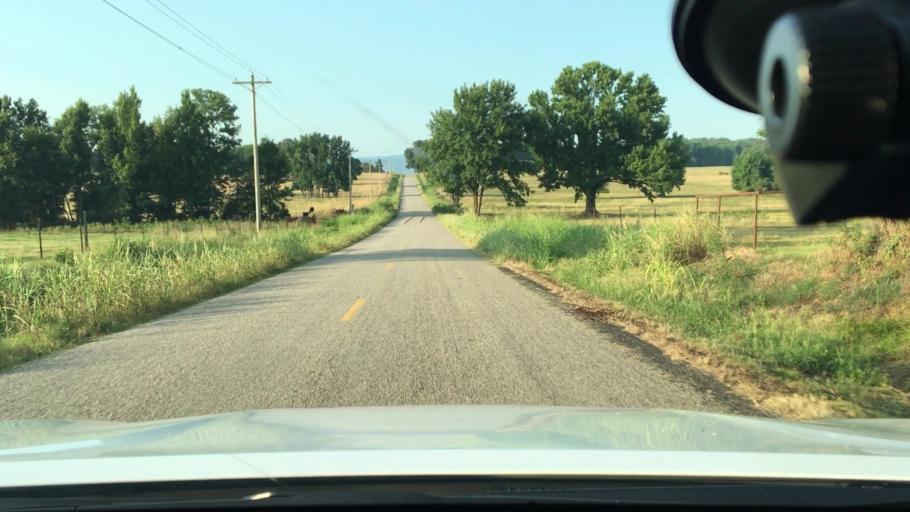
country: US
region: Arkansas
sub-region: Johnson County
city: Coal Hill
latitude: 35.3560
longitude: -93.6132
